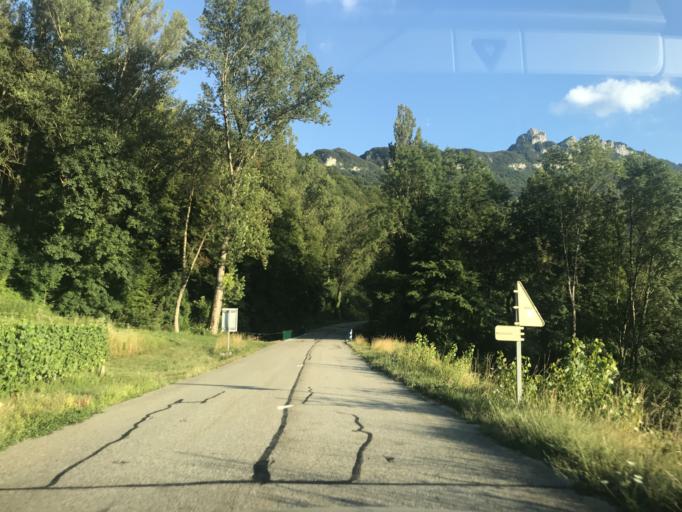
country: FR
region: Rhone-Alpes
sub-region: Departement de la Savoie
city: Le Bourget-du-Lac
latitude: 45.7008
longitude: 5.8345
